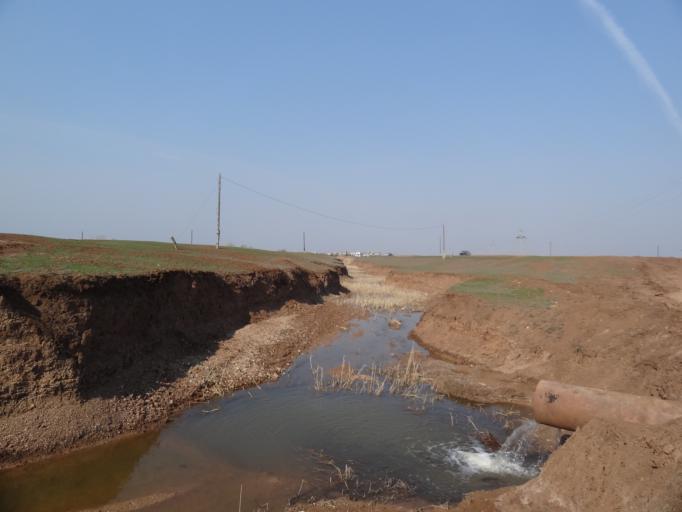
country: RU
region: Saratov
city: Privolzhskiy
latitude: 51.3085
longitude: 45.9682
